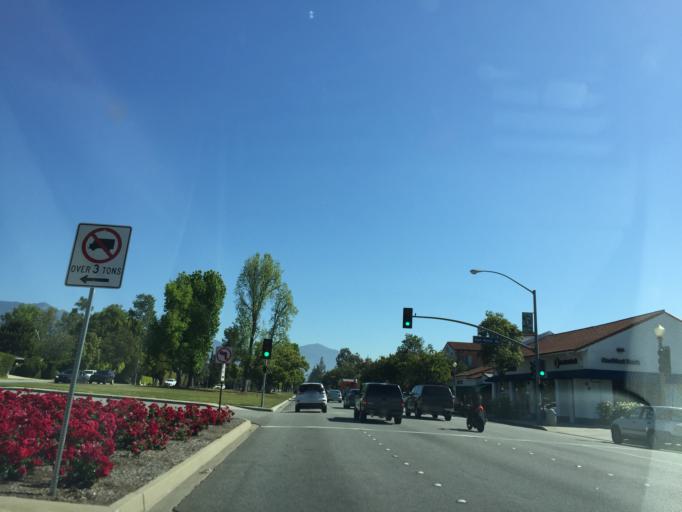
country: US
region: California
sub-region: Los Angeles County
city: Alhambra
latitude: 34.1116
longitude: -118.1271
